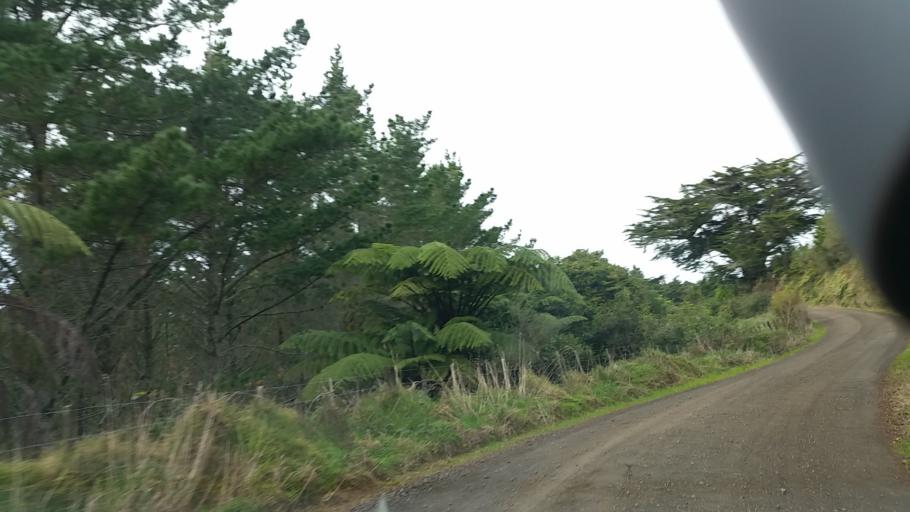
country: NZ
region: Taranaki
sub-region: New Plymouth District
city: Waitara
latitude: -39.0648
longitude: 174.3891
